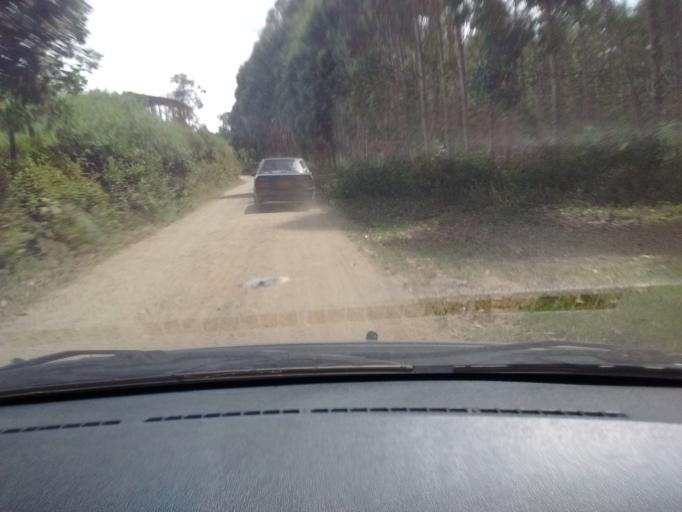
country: CO
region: Cauca
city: El Tambo
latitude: 2.4710
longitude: -76.8268
